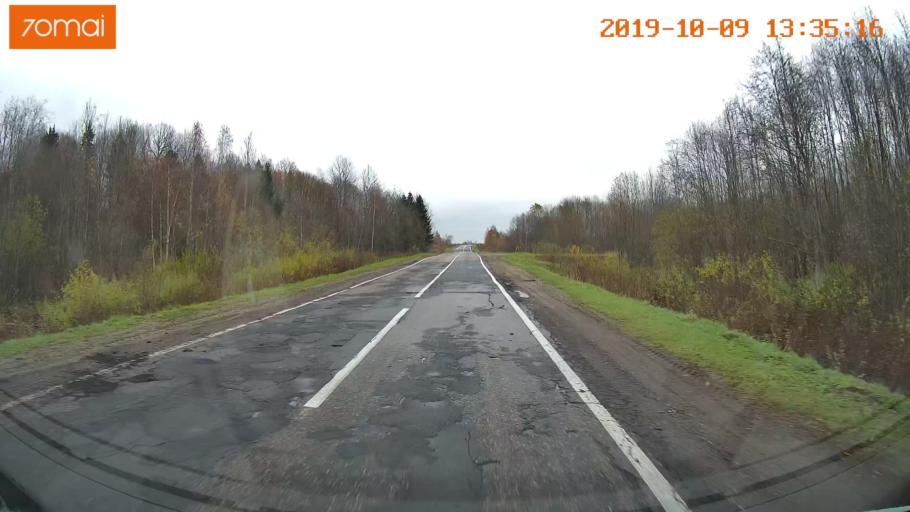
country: RU
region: Jaroslavl
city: Lyubim
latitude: 58.3352
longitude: 41.0751
